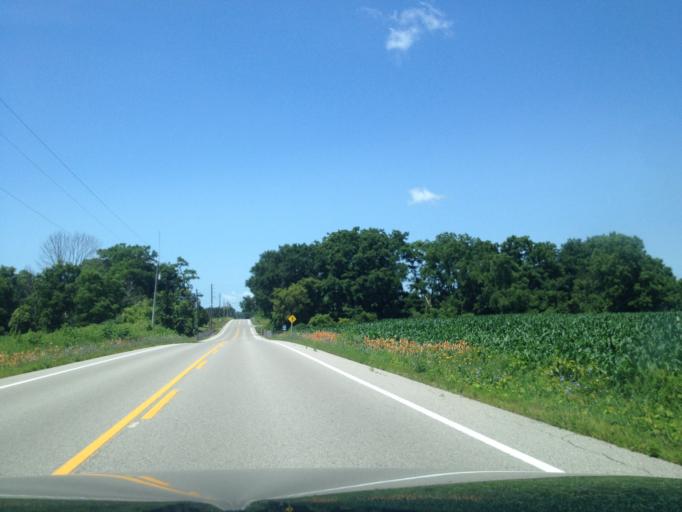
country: CA
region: Ontario
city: Norfolk County
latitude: 42.5826
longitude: -80.5954
